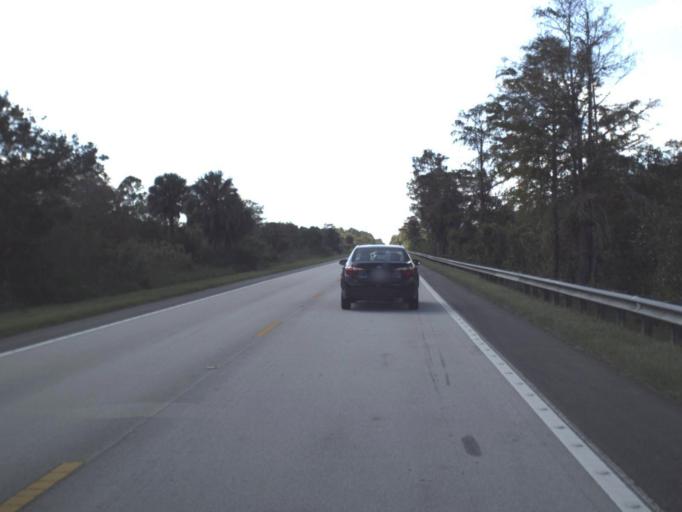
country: US
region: Florida
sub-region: Collier County
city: Lely Resort
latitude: 25.8699
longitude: -81.1608
